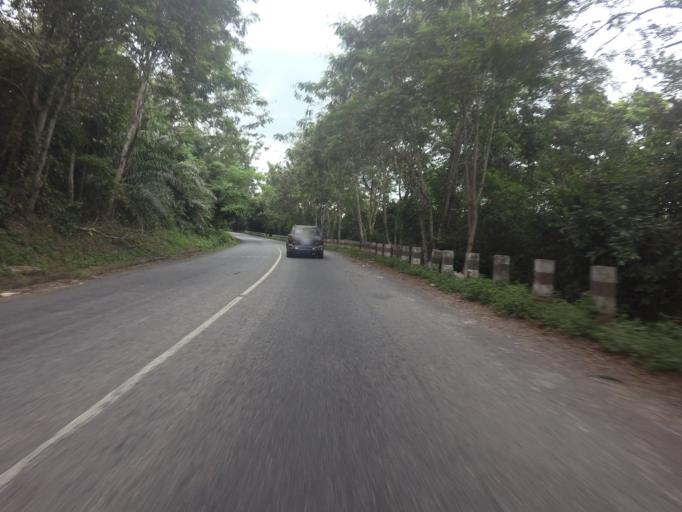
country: GH
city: Akropong
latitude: 5.9619
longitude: -0.1144
